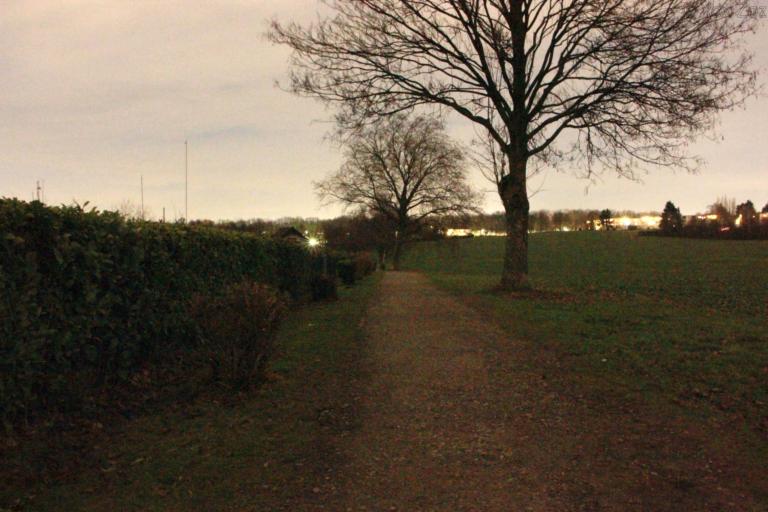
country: DE
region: North Rhine-Westphalia
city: Witten
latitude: 51.4896
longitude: 7.3203
